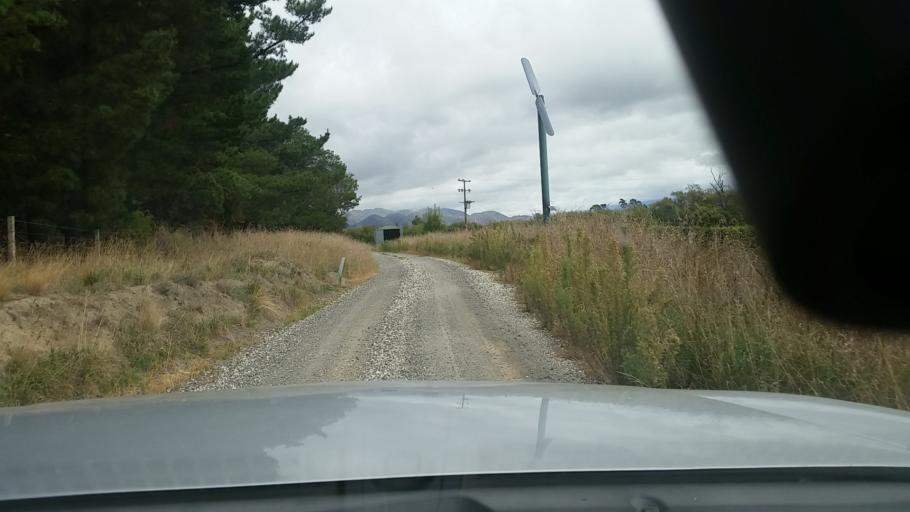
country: NZ
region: Marlborough
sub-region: Marlborough District
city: Blenheim
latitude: -41.6933
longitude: 174.1257
